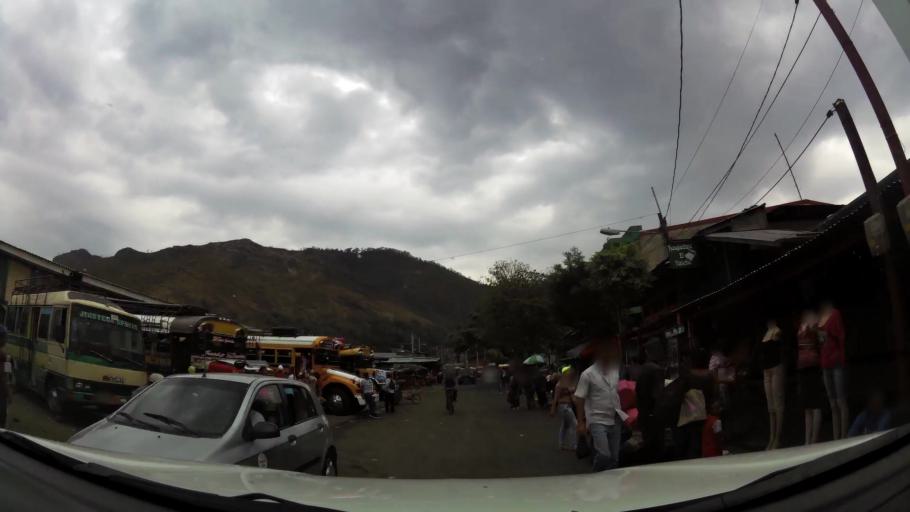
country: NI
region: Jinotega
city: Jinotega
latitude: 13.0934
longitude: -85.9974
